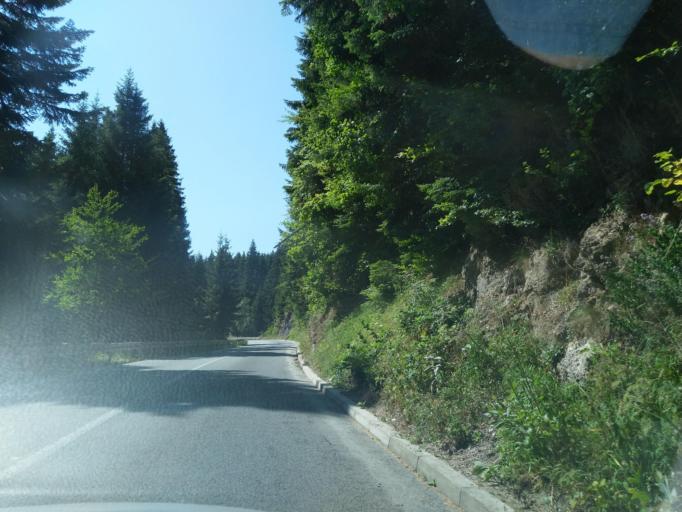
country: RS
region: Central Serbia
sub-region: Zlatiborski Okrug
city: Nova Varos
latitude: 43.4167
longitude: 19.8298
